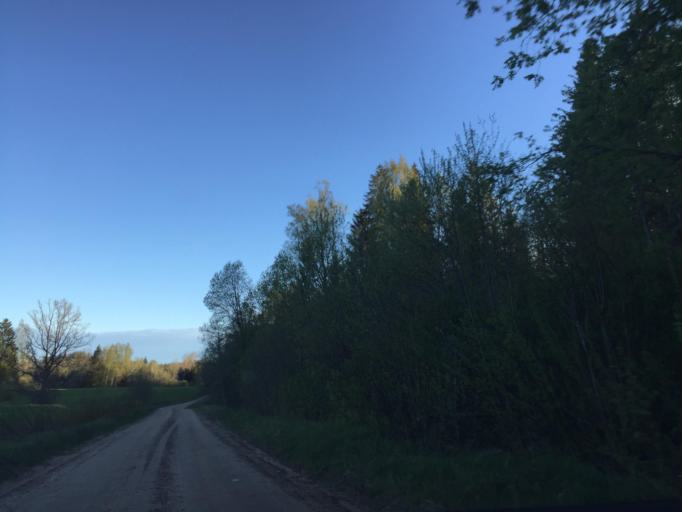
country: LV
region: Madonas Rajons
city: Madona
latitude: 56.8673
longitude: 25.9710
